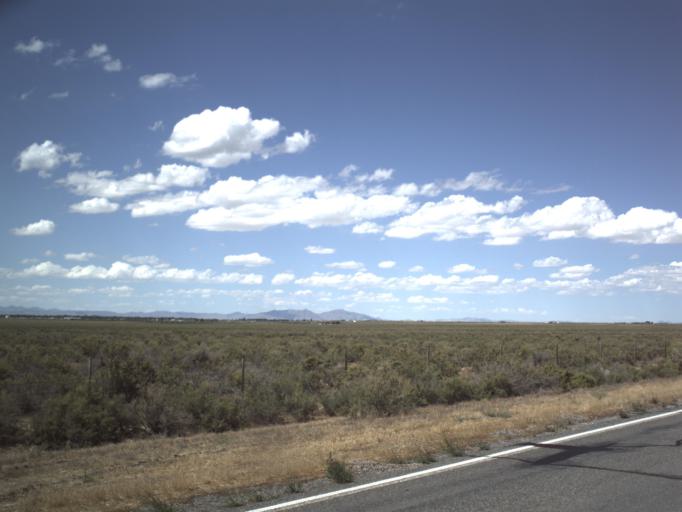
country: US
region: Utah
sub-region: Millard County
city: Delta
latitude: 39.3353
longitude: -112.4894
